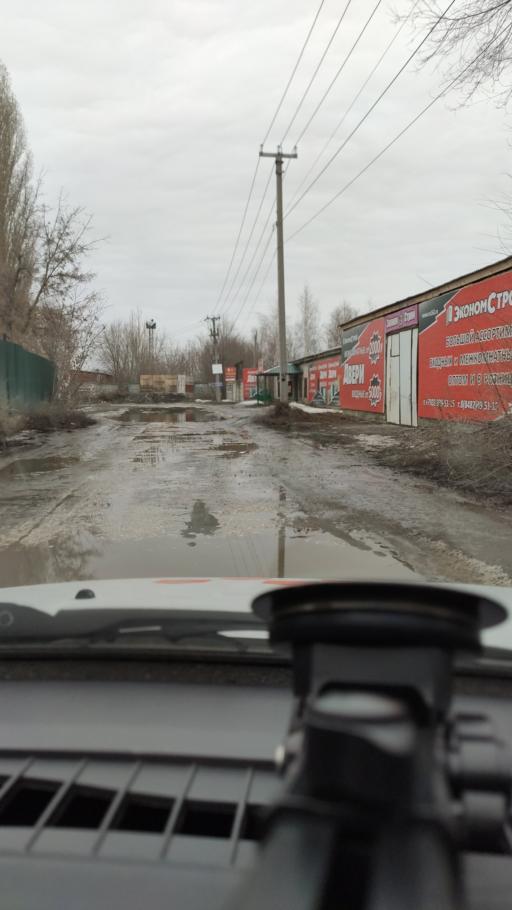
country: RU
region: Samara
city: Tol'yatti
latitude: 53.5355
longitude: 49.2601
